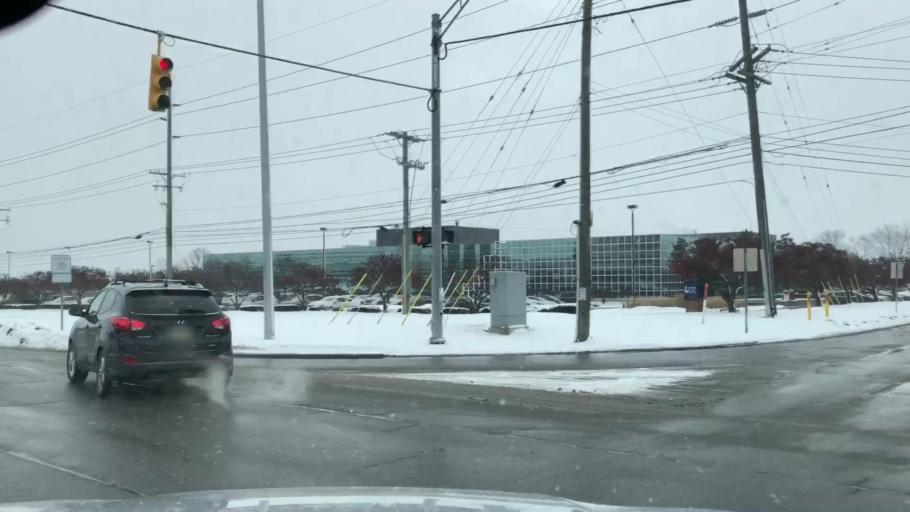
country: US
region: Michigan
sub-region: Wayne County
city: Plymouth
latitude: 42.4106
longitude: -83.4324
